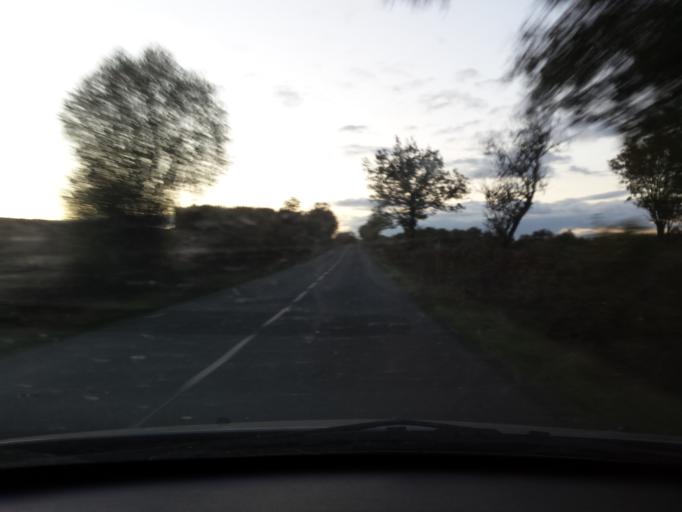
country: FR
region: Pays de la Loire
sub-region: Departement de la Vendee
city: Sainte-Cecile
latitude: 46.7483
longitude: -1.1353
